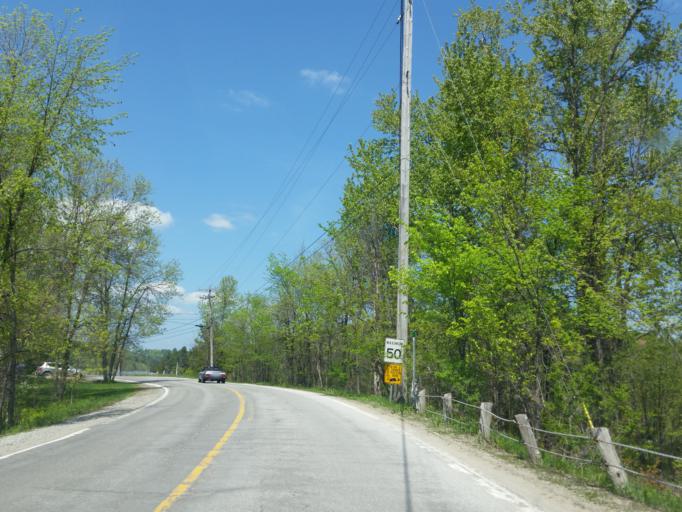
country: CA
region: Quebec
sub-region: Outaouais
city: Wakefield
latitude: 45.6009
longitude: -75.8837
